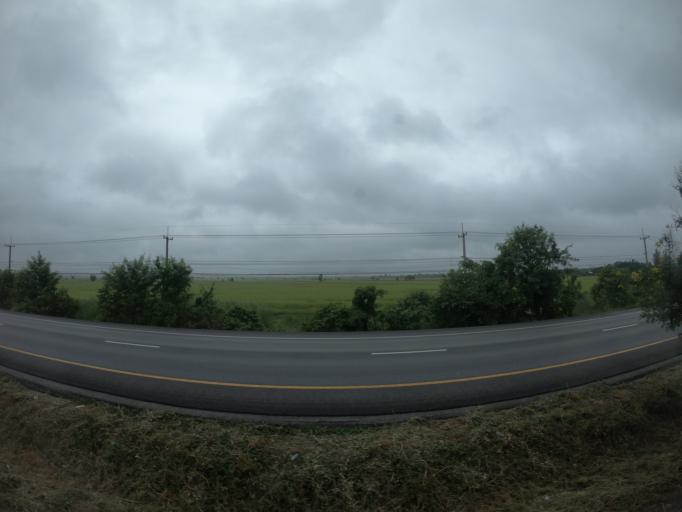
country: TH
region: Nakhon Ratchasima
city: Non Daeng
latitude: 15.3362
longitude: 102.4408
